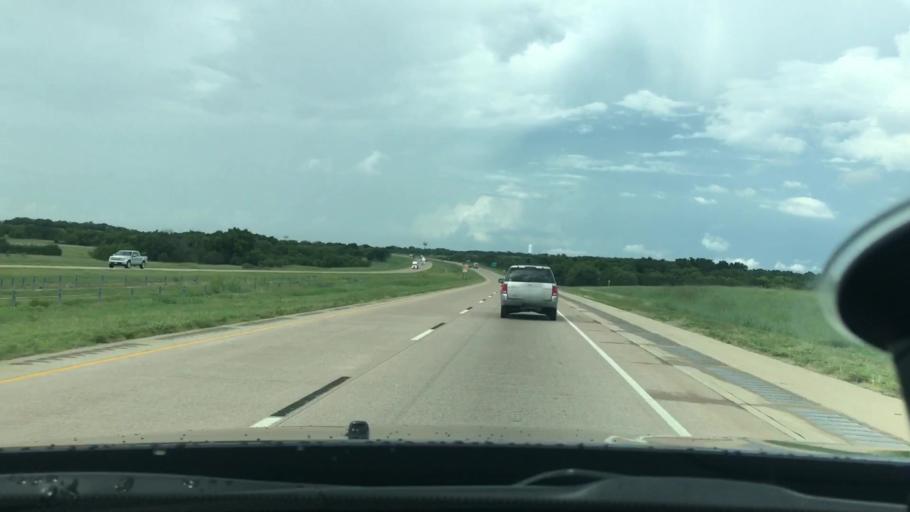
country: US
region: Oklahoma
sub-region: Garvin County
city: Pauls Valley
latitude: 34.6843
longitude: -97.2290
